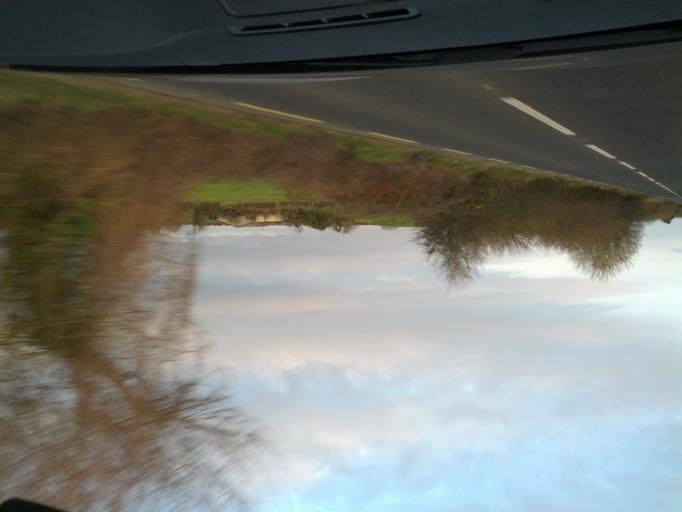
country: IE
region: Munster
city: Nenagh Bridge
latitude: 52.8875
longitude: -8.1921
